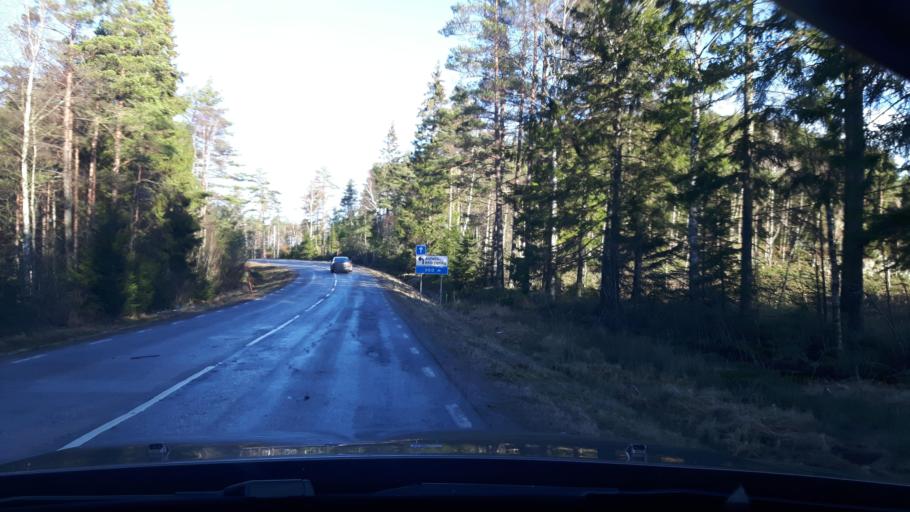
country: SE
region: Vaestra Goetaland
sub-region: Munkedals Kommun
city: Munkedal
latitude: 58.5153
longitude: 11.6838
